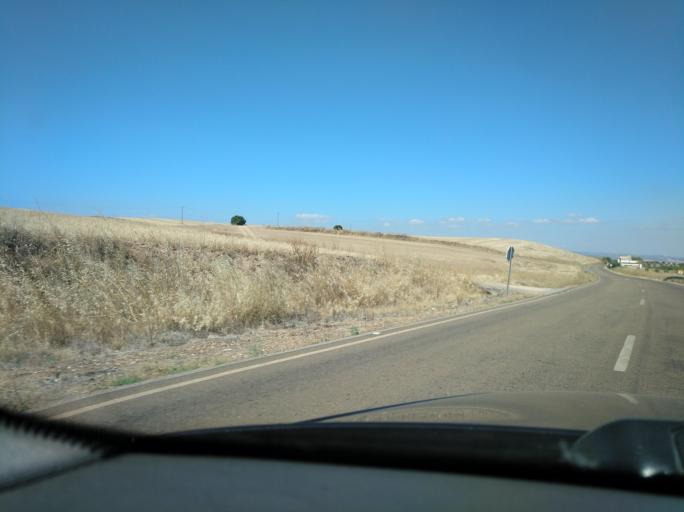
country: ES
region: Extremadura
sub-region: Provincia de Badajoz
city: Olivenza
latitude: 38.6957
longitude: -7.1292
